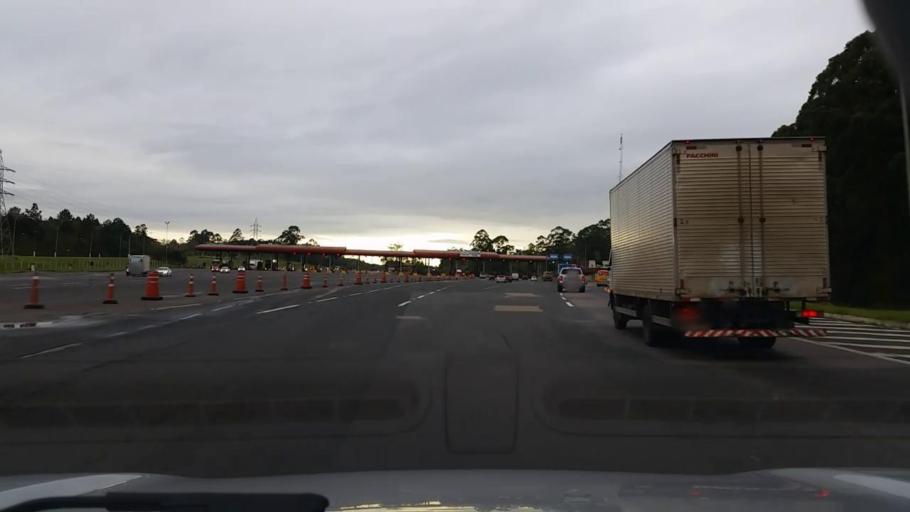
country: BR
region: Rio Grande do Sul
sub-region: Gravatai
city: Gravatai
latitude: -29.9548
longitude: -51.0342
